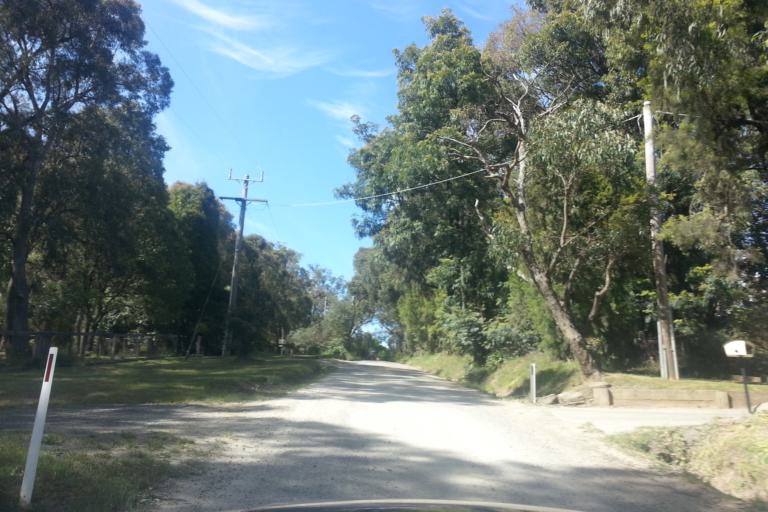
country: AU
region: Victoria
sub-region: Cardinia
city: Beaconsfield Upper
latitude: -37.9871
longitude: 145.4278
